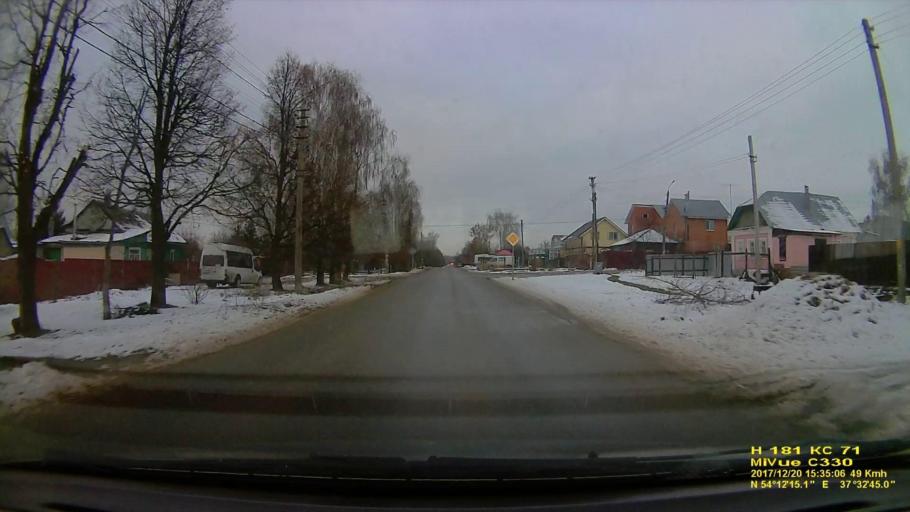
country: RU
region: Tula
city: Tula
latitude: 54.2041
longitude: 37.5459
